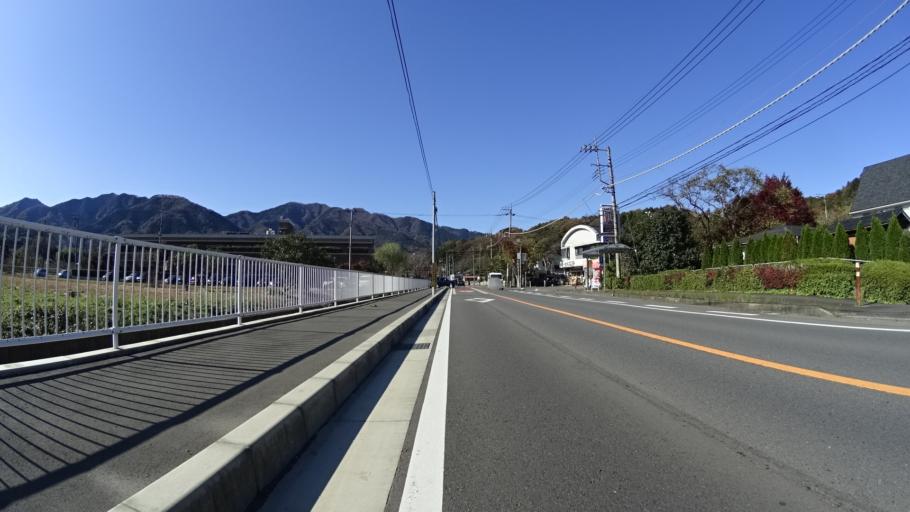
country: JP
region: Kanagawa
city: Zama
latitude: 35.5277
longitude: 139.3000
